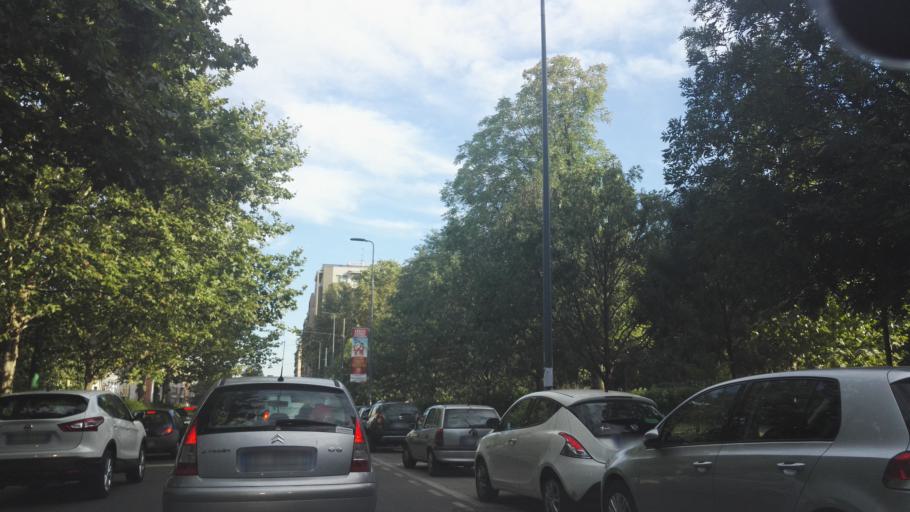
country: IT
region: Lombardy
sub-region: Citta metropolitana di Milano
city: Milano
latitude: 45.4536
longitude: 9.1534
